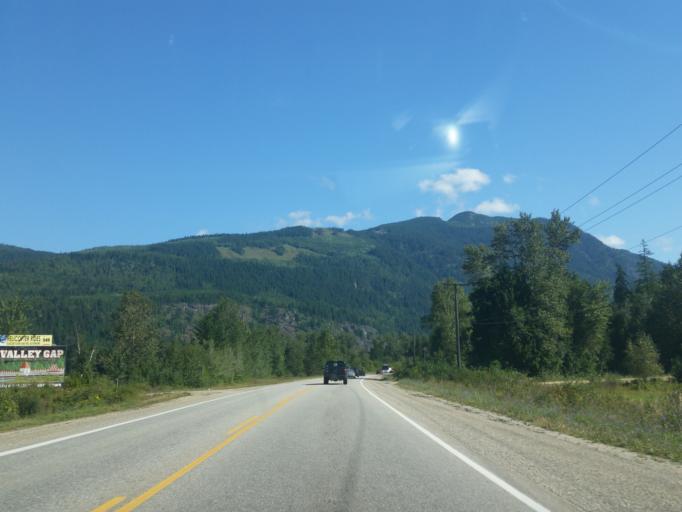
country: CA
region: British Columbia
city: Sicamous
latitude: 50.8699
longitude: -118.9266
